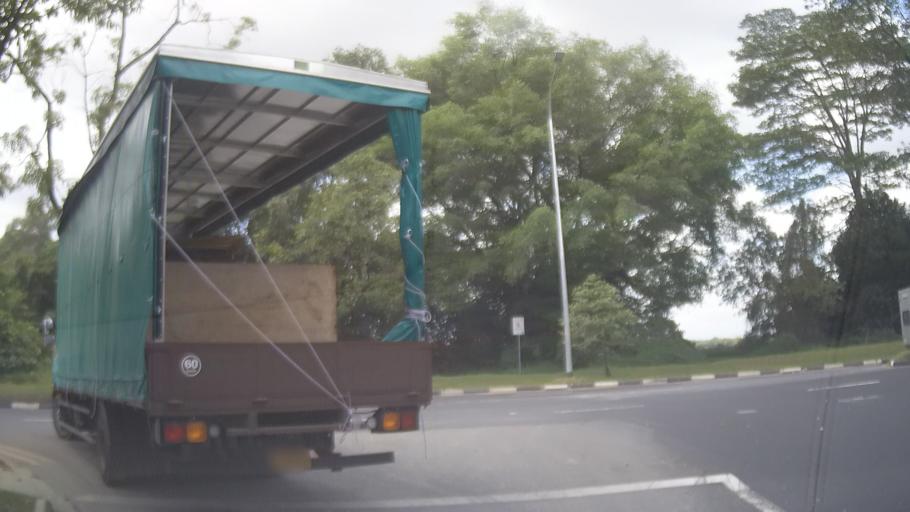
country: MY
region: Johor
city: Johor Bahru
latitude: 1.4288
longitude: 103.7475
